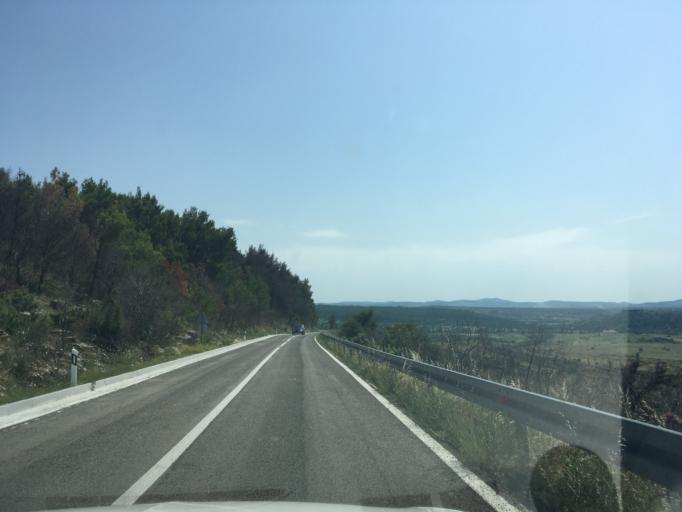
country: HR
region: Sibensko-Kniniska
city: Kistanje
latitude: 43.9447
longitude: 15.8335
